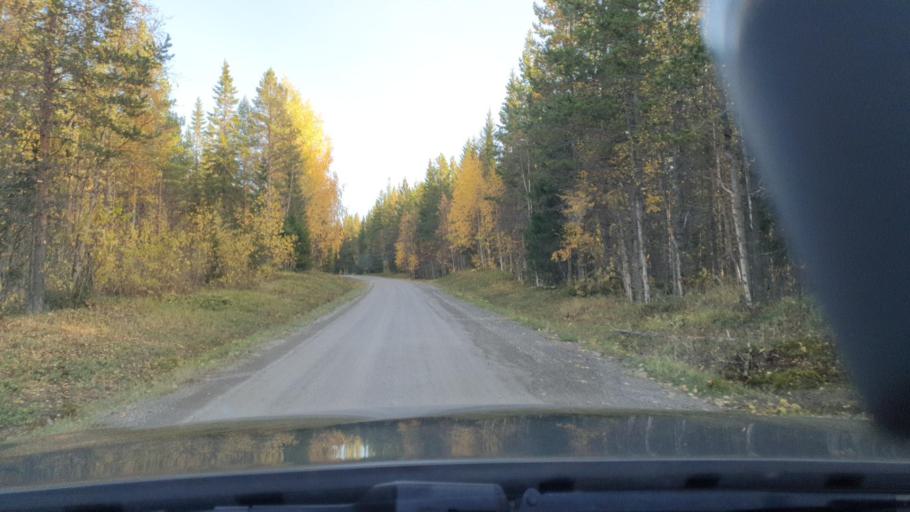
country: SE
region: Jaemtland
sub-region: Stroemsunds Kommun
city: Stroemsund
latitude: 63.5329
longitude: 15.6126
